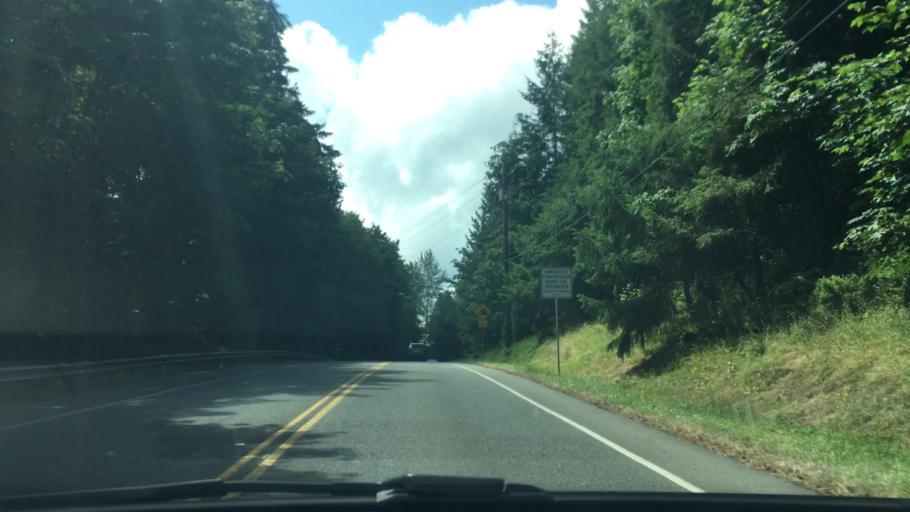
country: US
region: Washington
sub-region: King County
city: City of Sammamish
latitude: 47.5702
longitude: -122.0359
